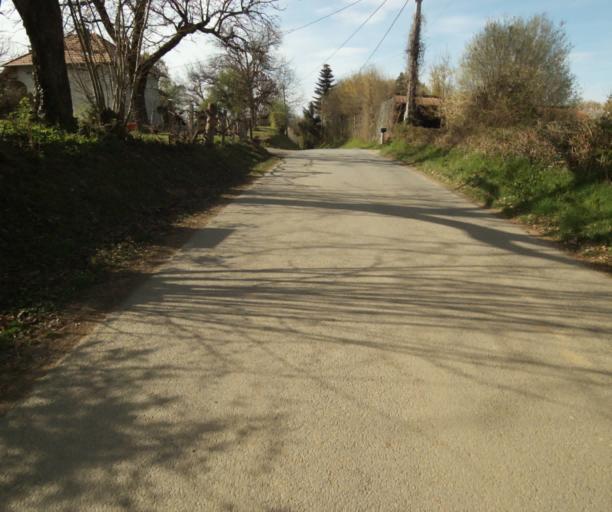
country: FR
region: Limousin
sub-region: Departement de la Correze
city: Naves
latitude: 45.3055
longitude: 1.7359
